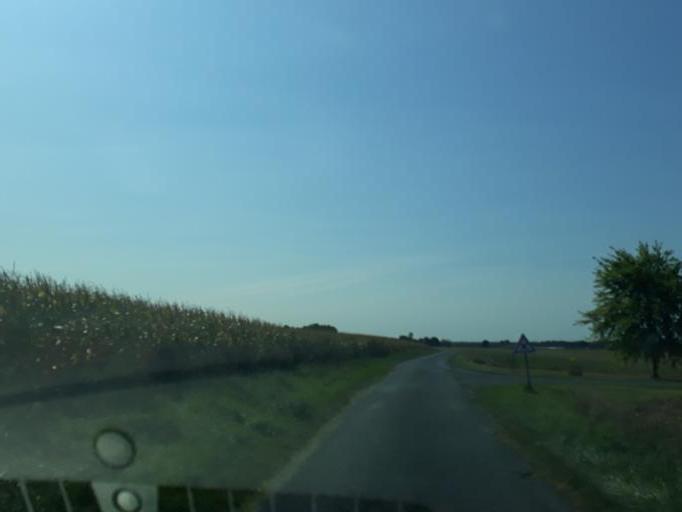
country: FR
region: Centre
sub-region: Departement de l'Indre
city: Chabris
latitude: 47.2672
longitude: 1.6032
